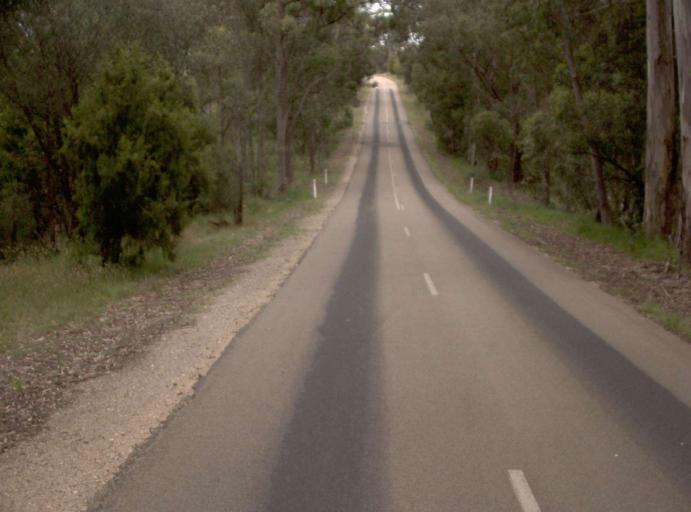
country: AU
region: Victoria
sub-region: East Gippsland
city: Bairnsdale
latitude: -37.7586
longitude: 147.5987
